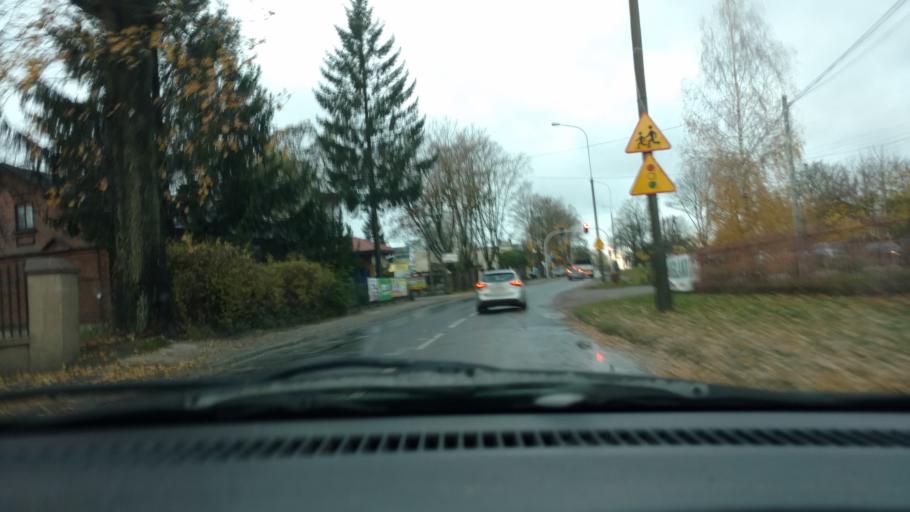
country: PL
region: Lodz Voivodeship
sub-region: Powiat lodzki wschodni
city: Andrespol
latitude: 51.7700
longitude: 19.5701
